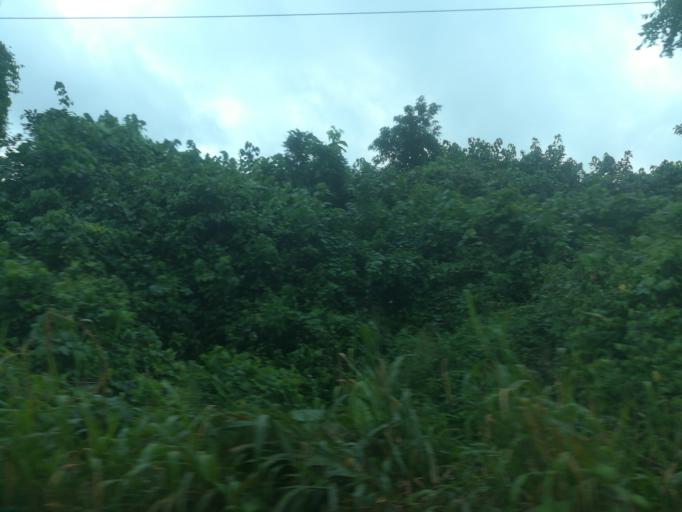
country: NG
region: Lagos
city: Ikorodu
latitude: 6.6629
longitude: 3.5967
